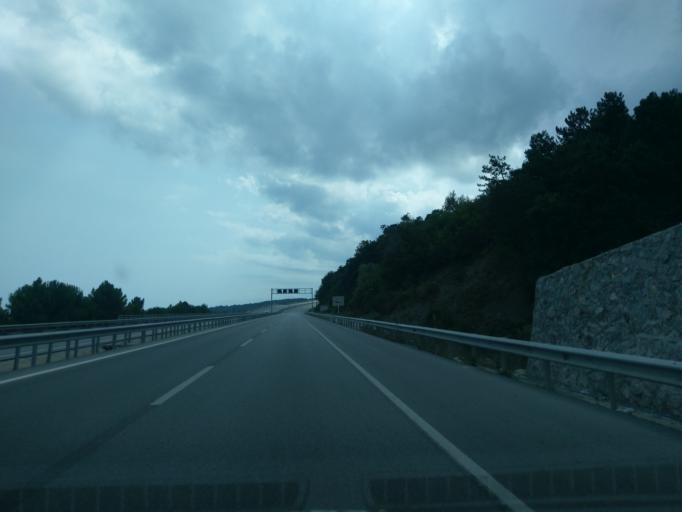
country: TR
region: Sinop
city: Gerze
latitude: 41.8282
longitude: 35.1627
